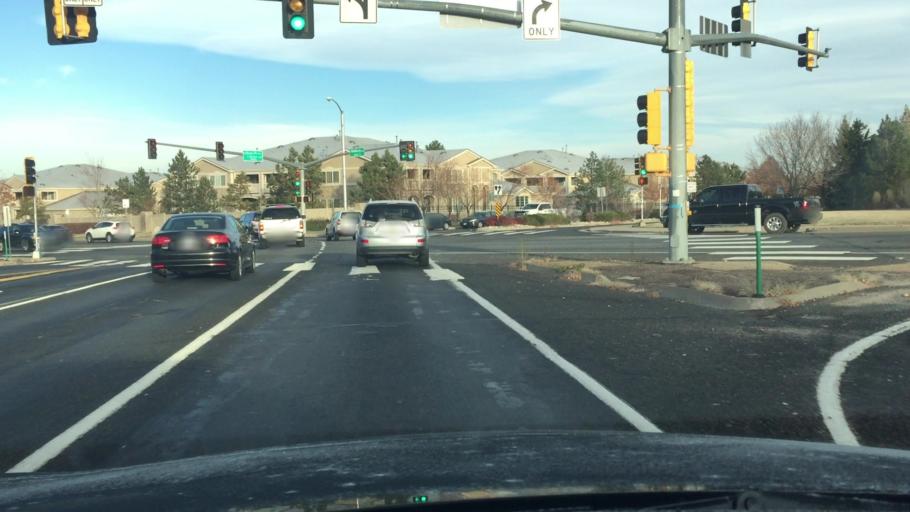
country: US
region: Colorado
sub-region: Arapahoe County
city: Dove Valley
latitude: 39.6383
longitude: -104.8223
